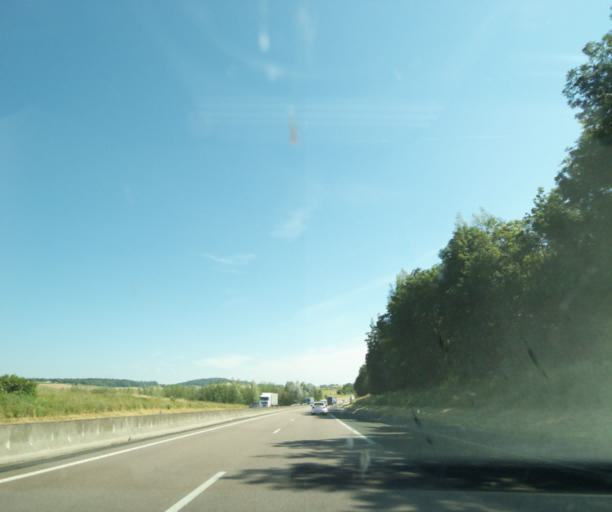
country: FR
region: Lorraine
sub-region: Departement des Vosges
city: Chatenois
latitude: 48.3470
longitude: 5.8554
